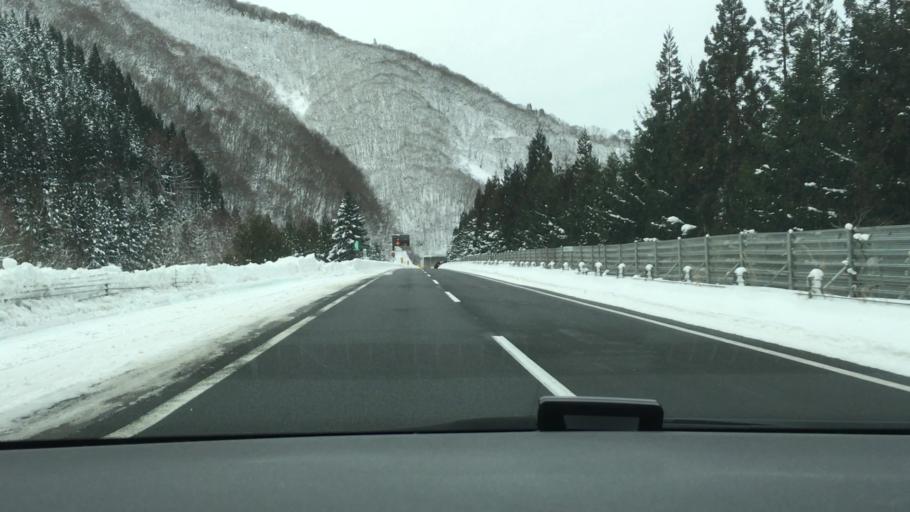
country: JP
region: Akita
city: Hanawa
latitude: 40.1146
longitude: 140.8719
